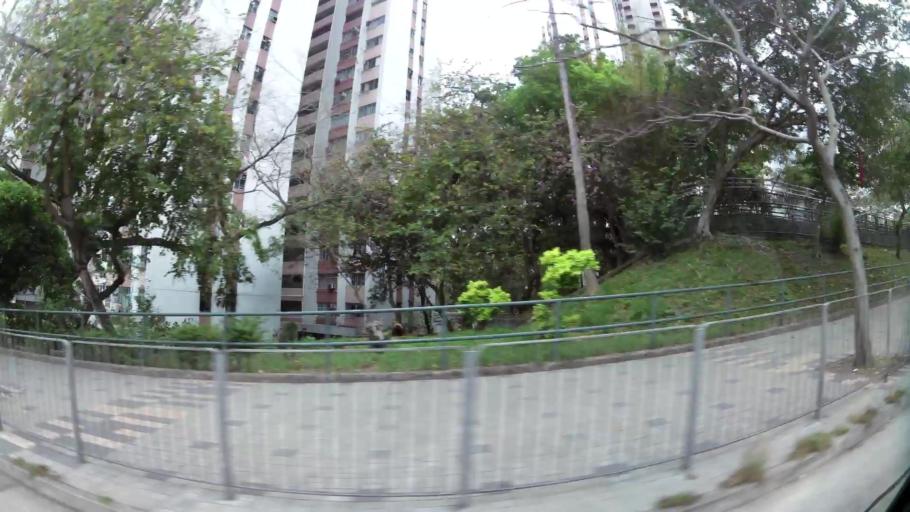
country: HK
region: Kowloon City
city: Kowloon
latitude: 22.3327
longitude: 114.2134
